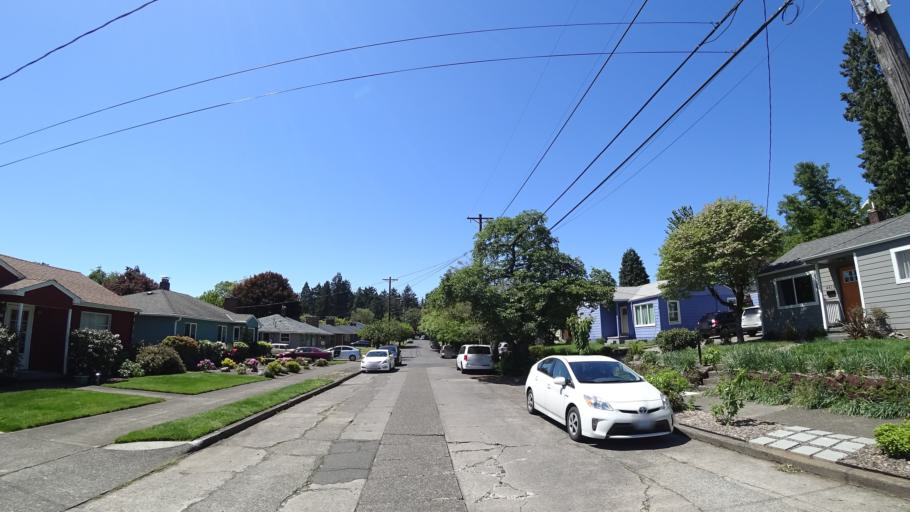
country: US
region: Oregon
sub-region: Multnomah County
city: Lents
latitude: 45.5003
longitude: -122.6132
